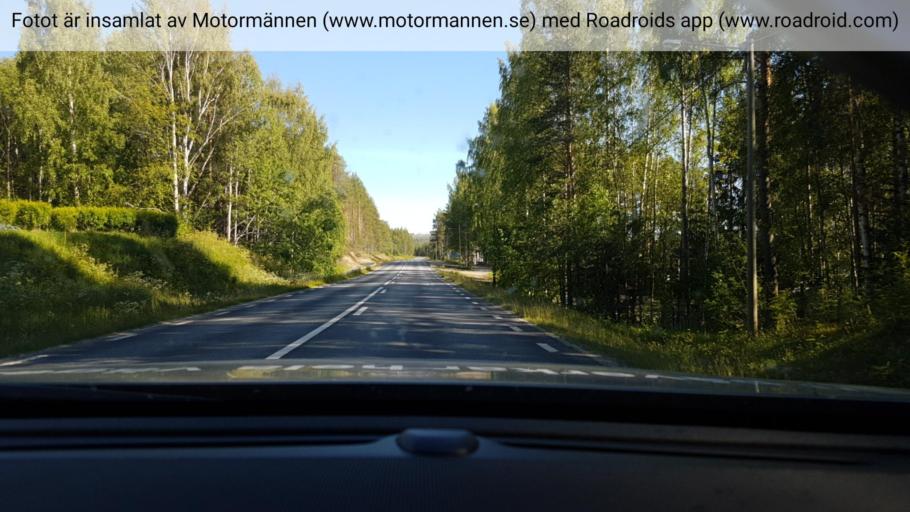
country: SE
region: Vaesterbotten
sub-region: Lycksele Kommun
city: Lycksele
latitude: 64.5394
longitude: 18.7545
